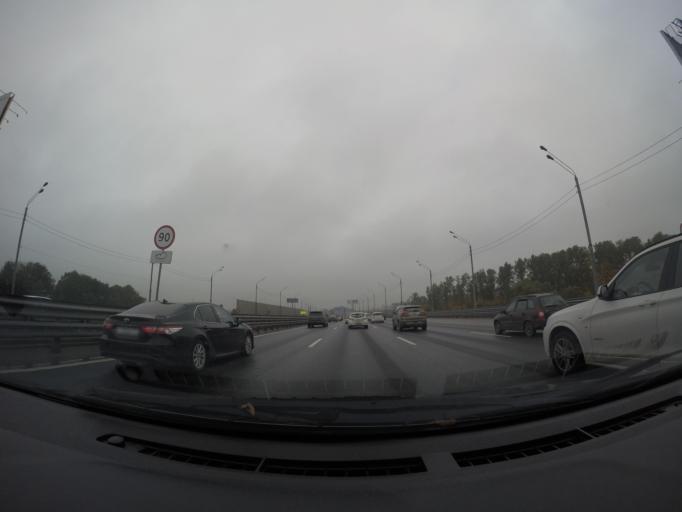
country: RU
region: Moskovskaya
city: Krasnogorsk
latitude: 55.8028
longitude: 37.3178
